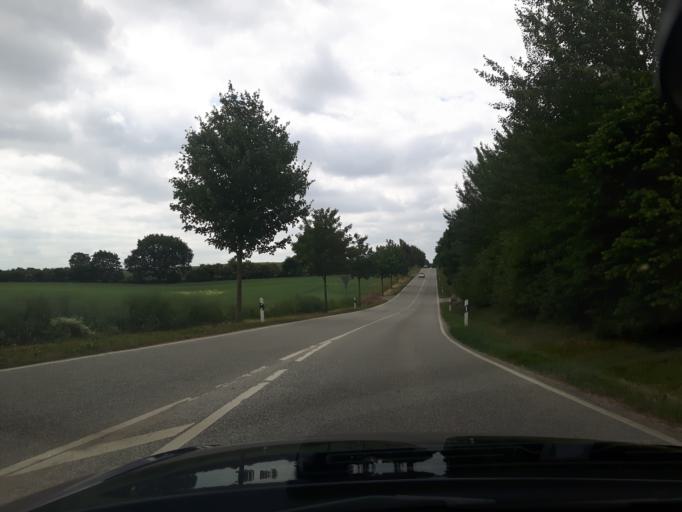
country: DE
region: Schleswig-Holstein
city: Altenkrempe
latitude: 54.1013
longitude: 10.8525
